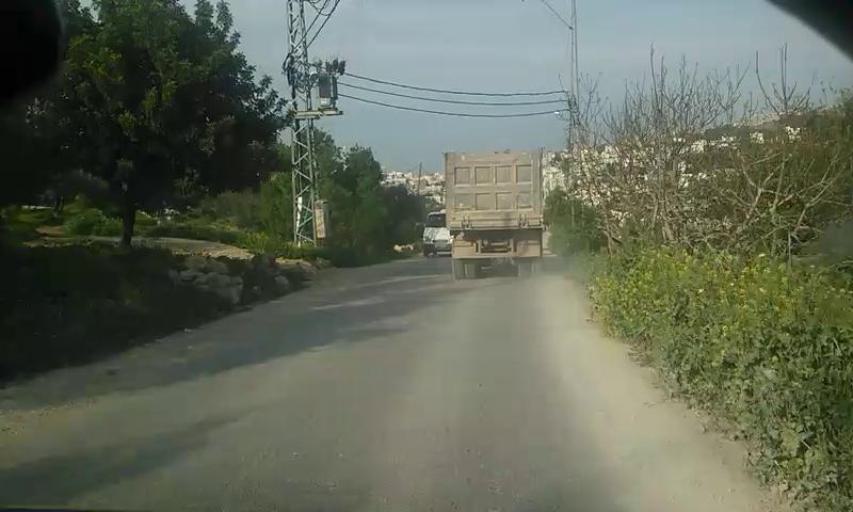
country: PS
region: West Bank
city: Bayt Ula
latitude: 31.5885
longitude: 35.0254
